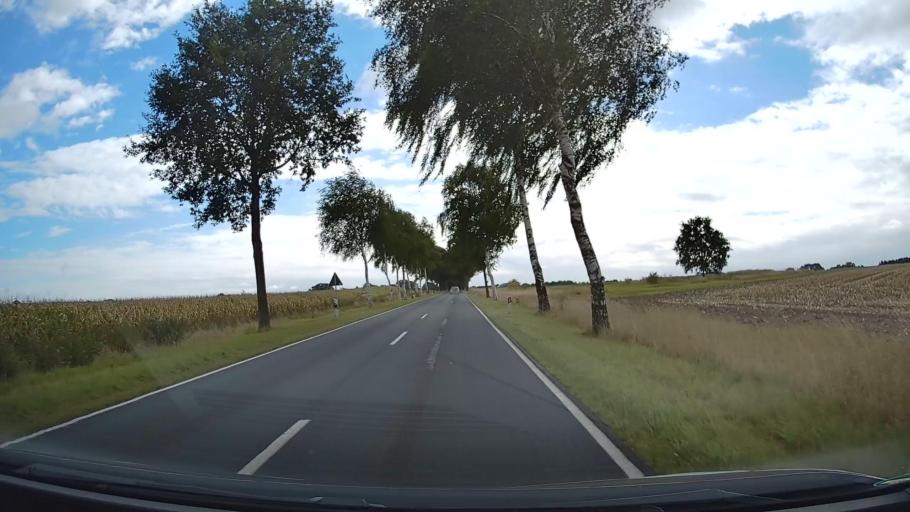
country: DE
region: Lower Saxony
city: Rhade
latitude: 53.3175
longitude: 9.1282
